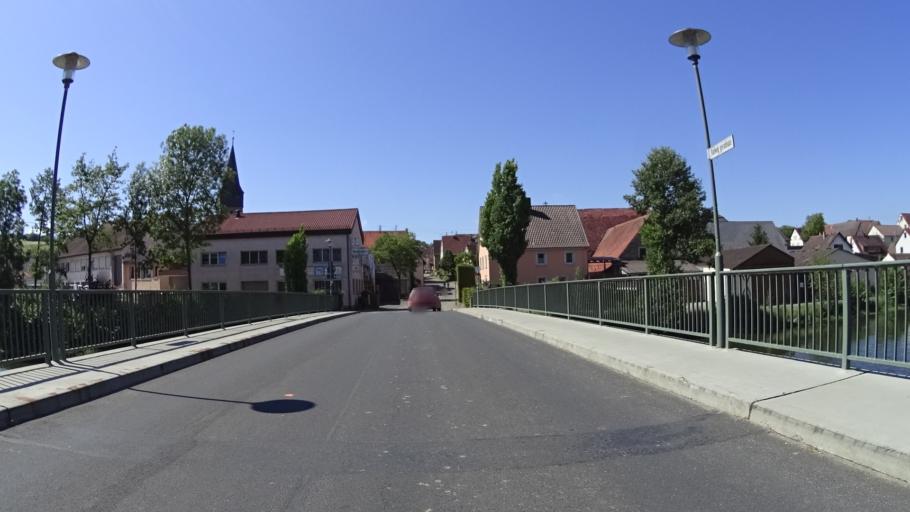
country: DE
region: Baden-Wuerttemberg
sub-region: Regierungsbezirk Stuttgart
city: Weikersheim
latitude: 49.4711
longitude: 9.8731
